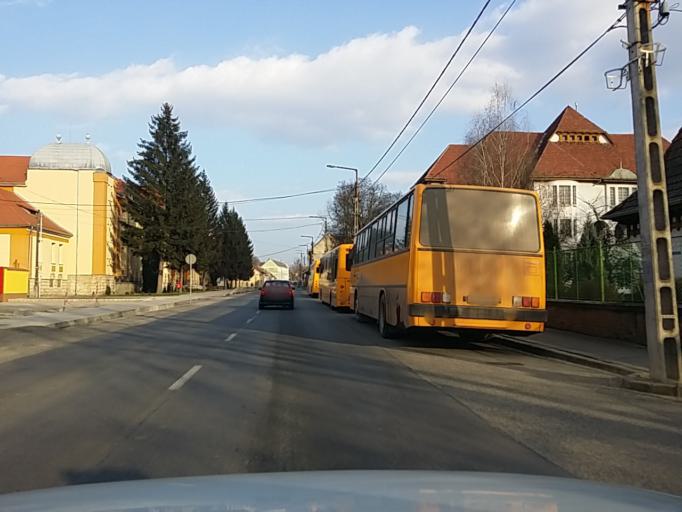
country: HU
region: Borsod-Abauj-Zemplen
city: Putnok
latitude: 48.2960
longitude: 20.4260
